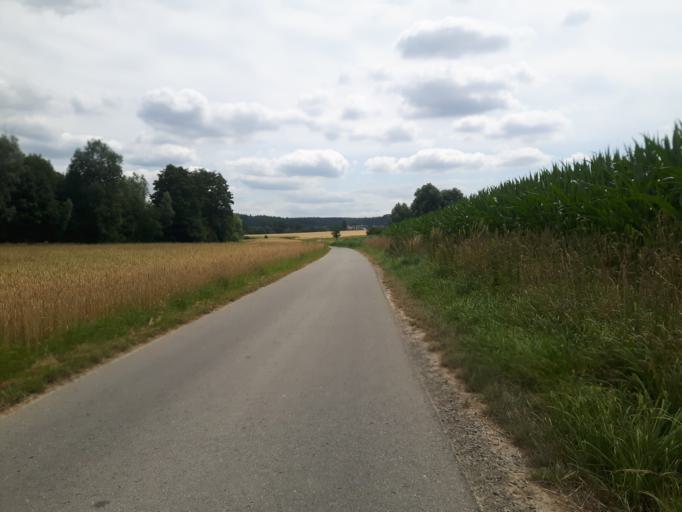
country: DE
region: Baden-Wuerttemberg
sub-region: Regierungsbezirk Stuttgart
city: Eppingen
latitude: 49.1142
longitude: 8.8908
